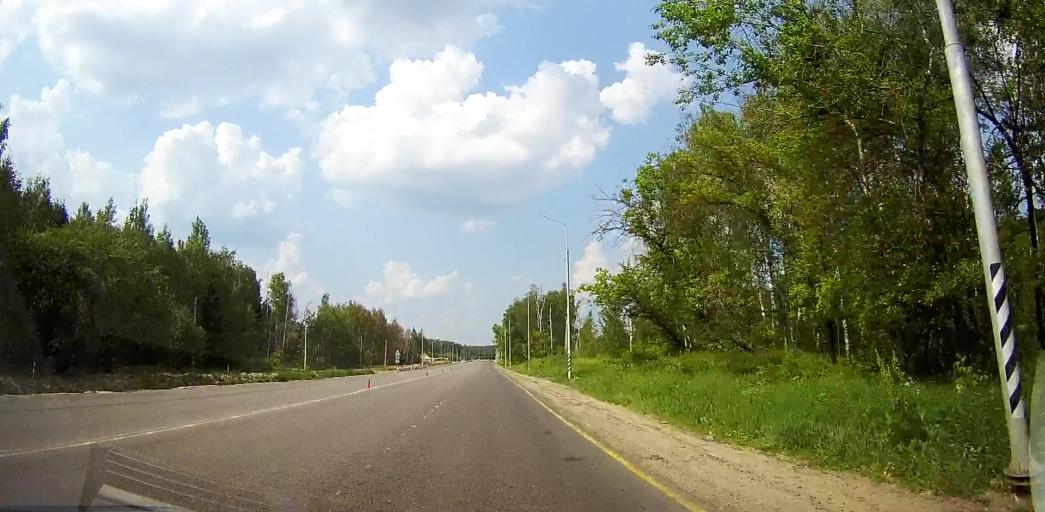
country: RU
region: Moskovskaya
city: Mikhnevo
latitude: 55.0680
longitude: 37.9529
